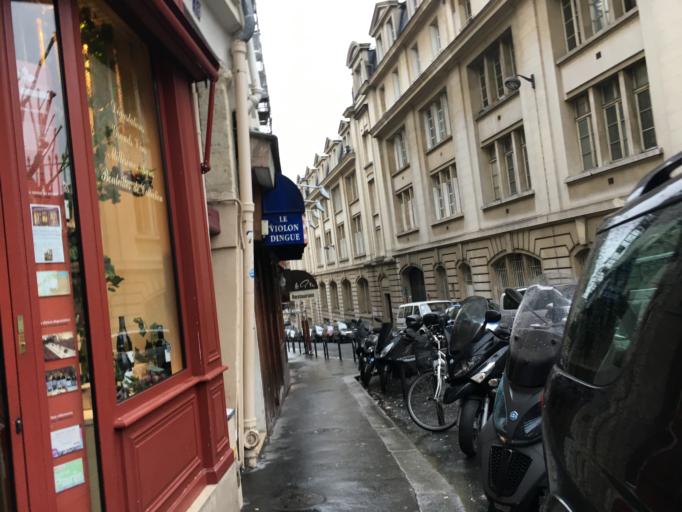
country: FR
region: Ile-de-France
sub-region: Paris
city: Paris
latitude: 48.8476
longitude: 2.3485
